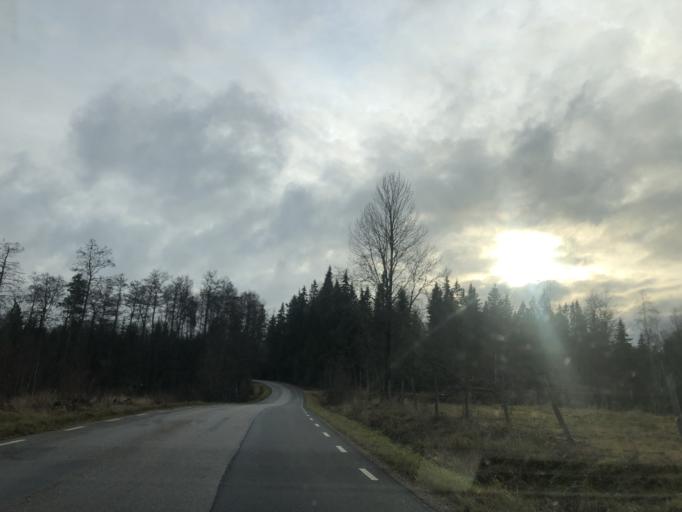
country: SE
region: Vaestra Goetaland
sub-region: Boras Kommun
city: Dalsjofors
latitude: 57.8184
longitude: 13.1967
